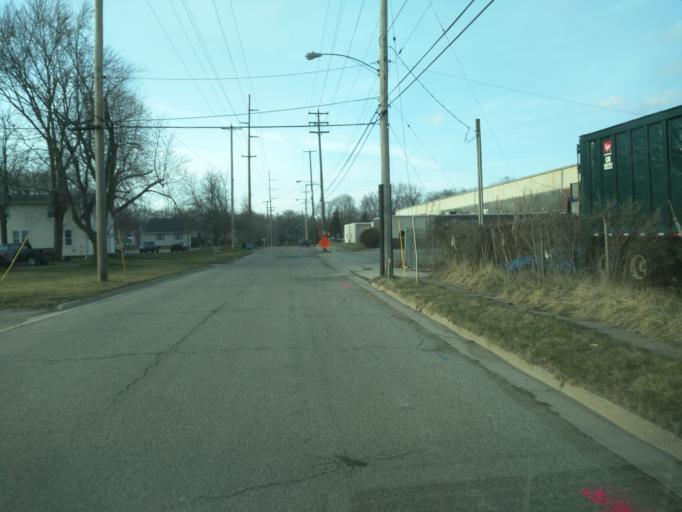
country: US
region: Michigan
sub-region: Ingham County
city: Edgemont Park
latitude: 42.7544
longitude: -84.5792
